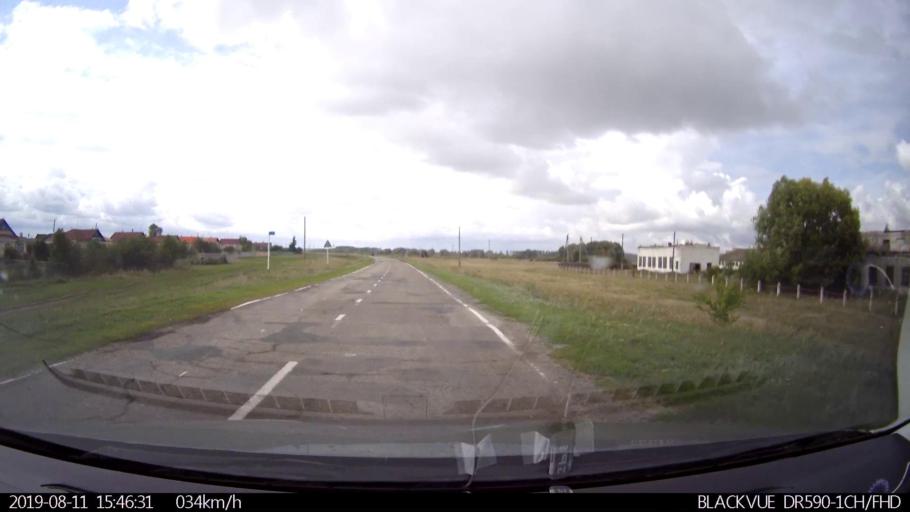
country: RU
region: Ulyanovsk
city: Ignatovka
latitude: 53.8827
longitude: 47.6559
